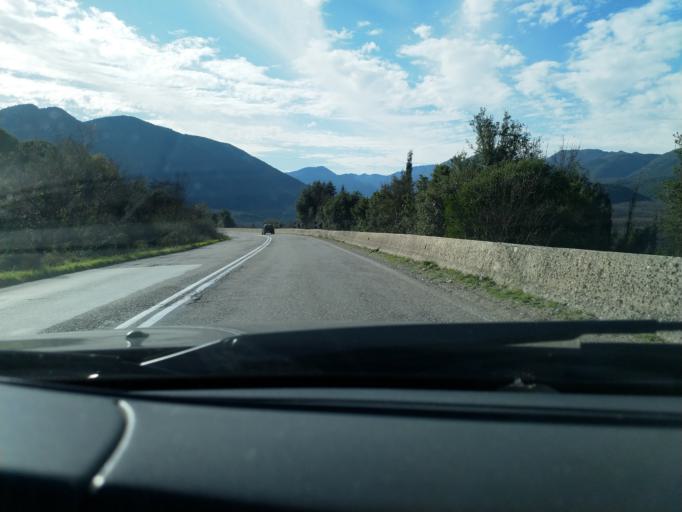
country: GR
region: Epirus
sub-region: Nomos Ioanninon
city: Agia Kyriaki
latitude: 39.4682
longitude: 20.8764
